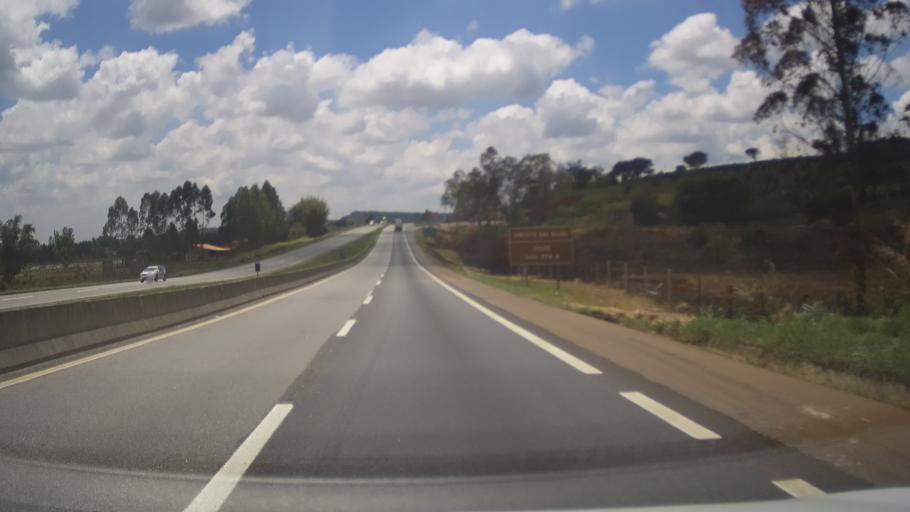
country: BR
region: Minas Gerais
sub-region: Campanha
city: Campanha
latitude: -21.7902
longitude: -45.4460
